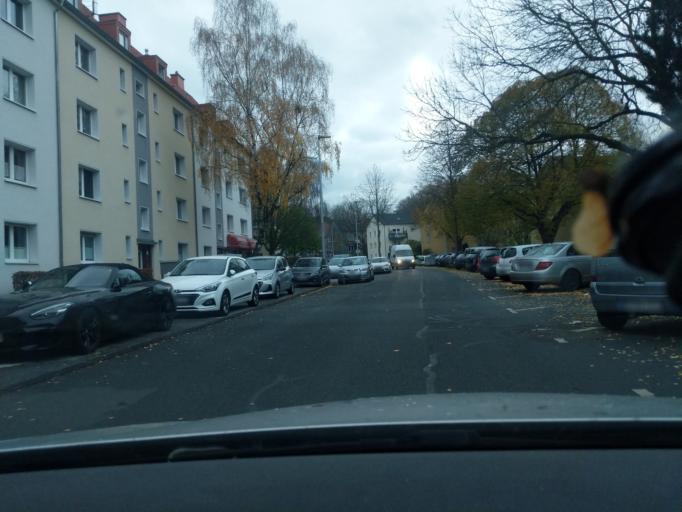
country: DE
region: North Rhine-Westphalia
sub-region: Regierungsbezirk Arnsberg
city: Dortmund
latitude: 51.5055
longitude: 7.4464
